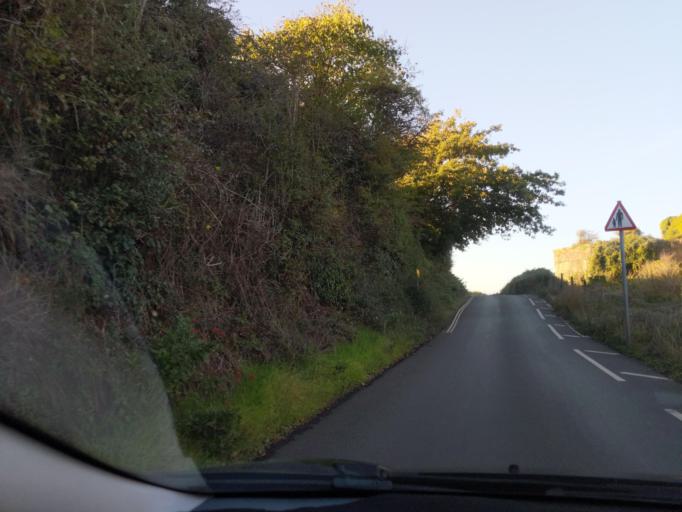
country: GB
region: England
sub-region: Plymouth
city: Plymouth
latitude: 50.3547
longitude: -4.1207
